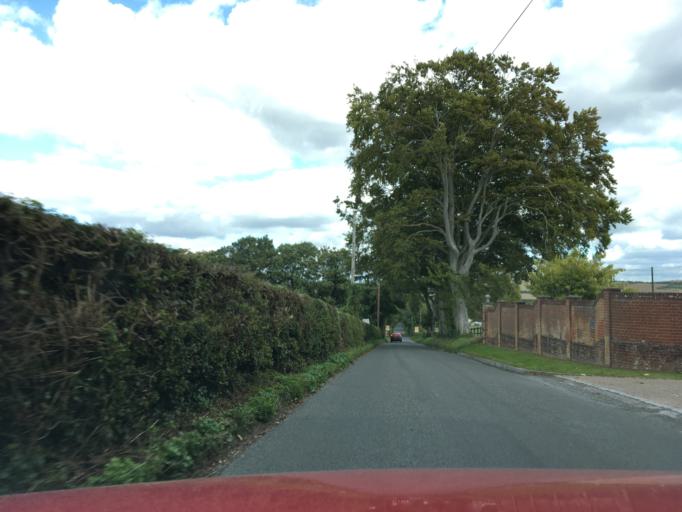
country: GB
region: England
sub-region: Wiltshire
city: Salisbury
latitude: 51.0945
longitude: -1.7830
